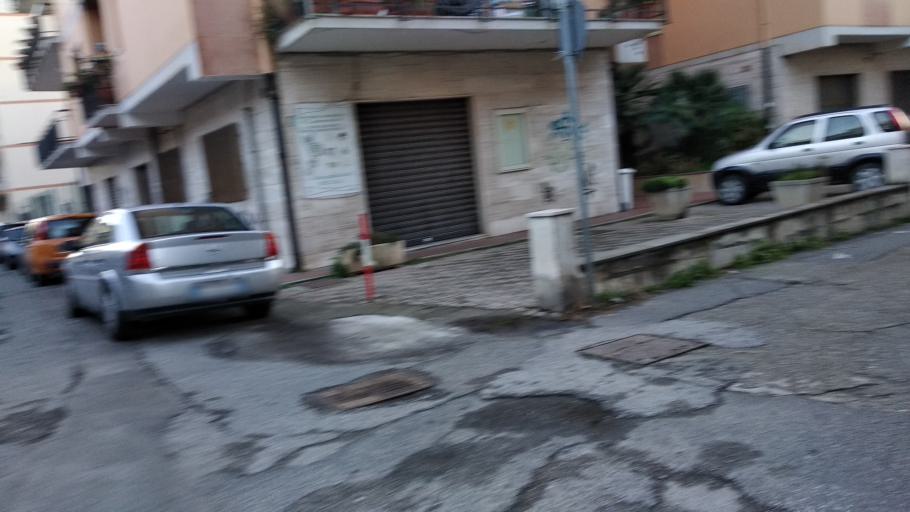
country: IT
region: Calabria
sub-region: Provincia di Catanzaro
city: Barone
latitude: 38.8275
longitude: 16.6262
